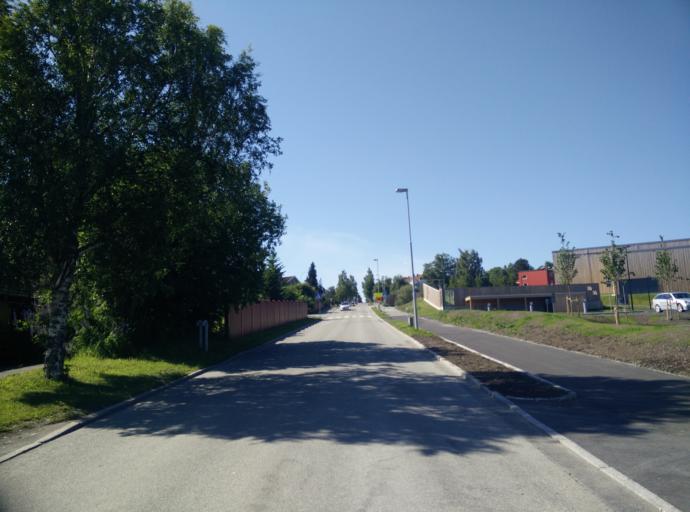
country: NO
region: Sor-Trondelag
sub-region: Trondheim
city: Trondheim
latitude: 63.4142
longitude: 10.3699
